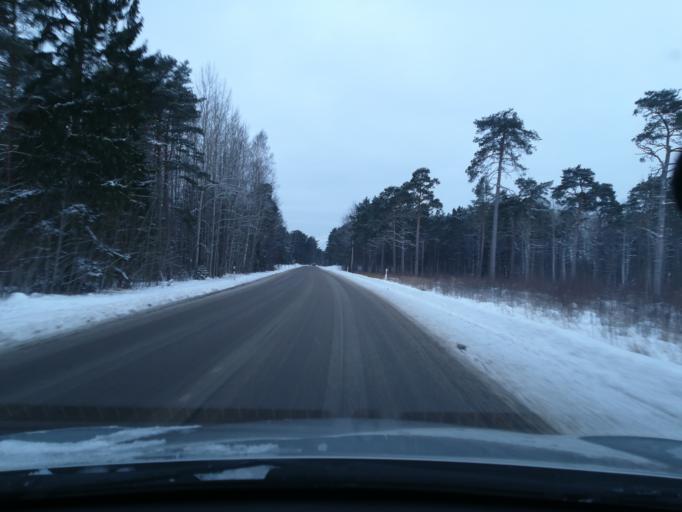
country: EE
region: Harju
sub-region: Keila linn
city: Keila
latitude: 59.4023
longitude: 24.3012
